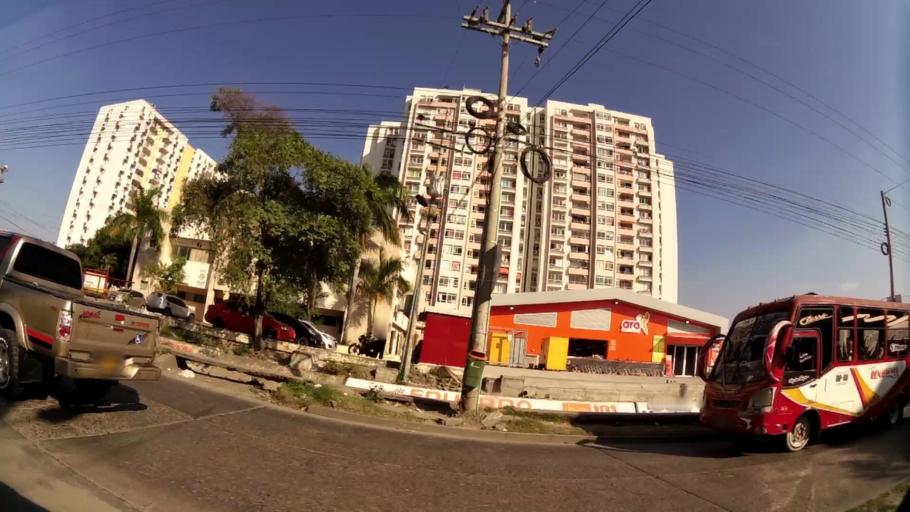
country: CO
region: Bolivar
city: Cartagena
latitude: 10.3888
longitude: -75.4813
